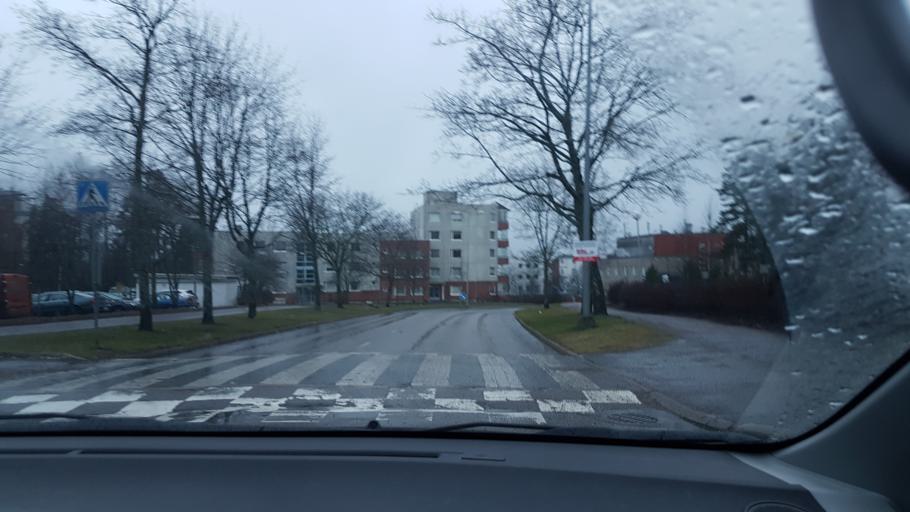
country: FI
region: Uusimaa
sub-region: Helsinki
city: Vantaa
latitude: 60.2424
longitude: 25.1145
